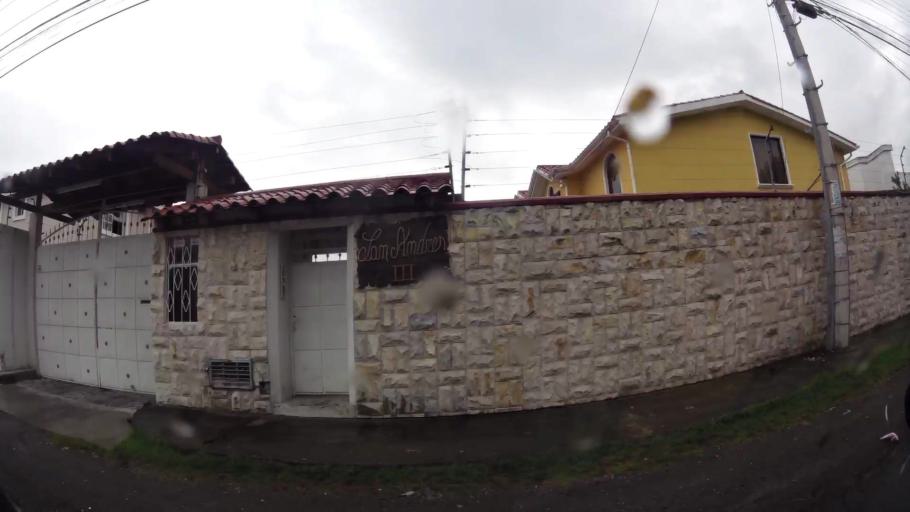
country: EC
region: Pichincha
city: Sangolqui
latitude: -0.2846
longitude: -78.4540
